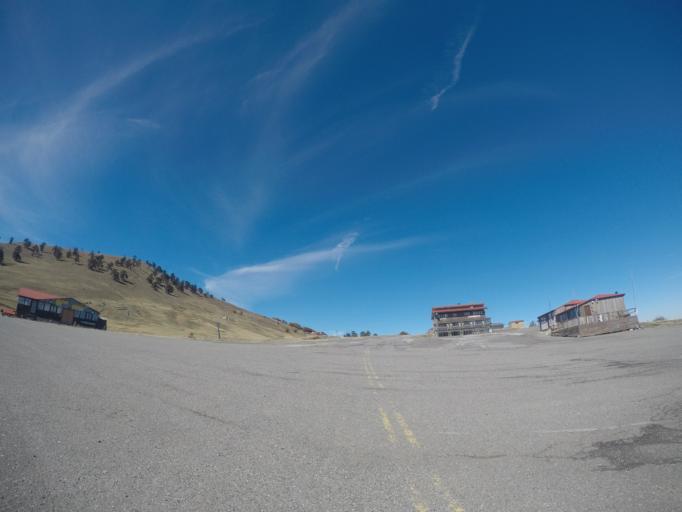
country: GR
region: Epirus
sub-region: Nomos Ioanninon
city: Metsovo
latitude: 40.0584
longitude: 21.0838
